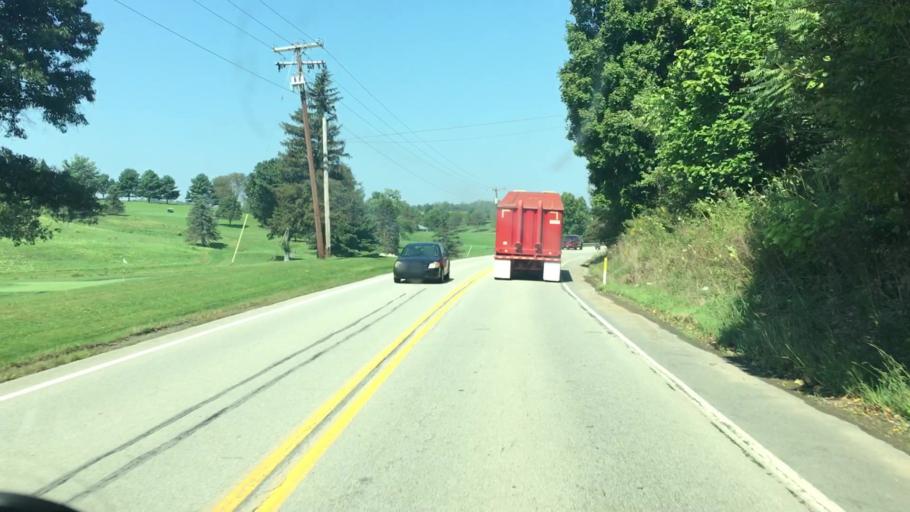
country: US
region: Pennsylvania
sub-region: Washington County
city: Washington
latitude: 40.1092
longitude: -80.2939
